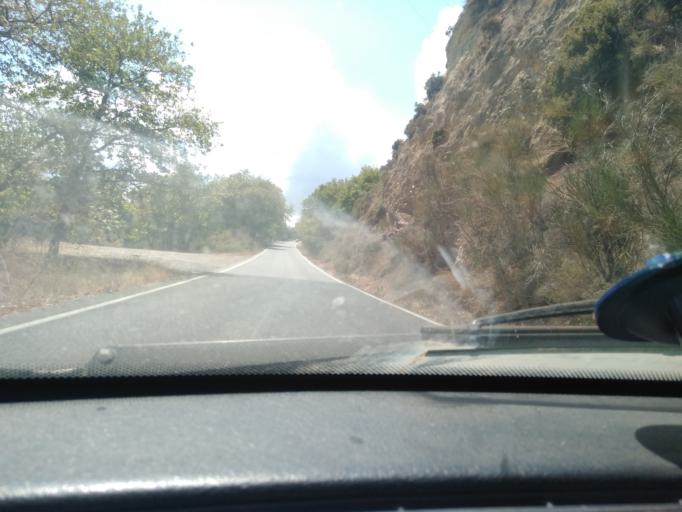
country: GR
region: Crete
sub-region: Nomos Lasithiou
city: Siteia
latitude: 35.1292
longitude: 26.0658
